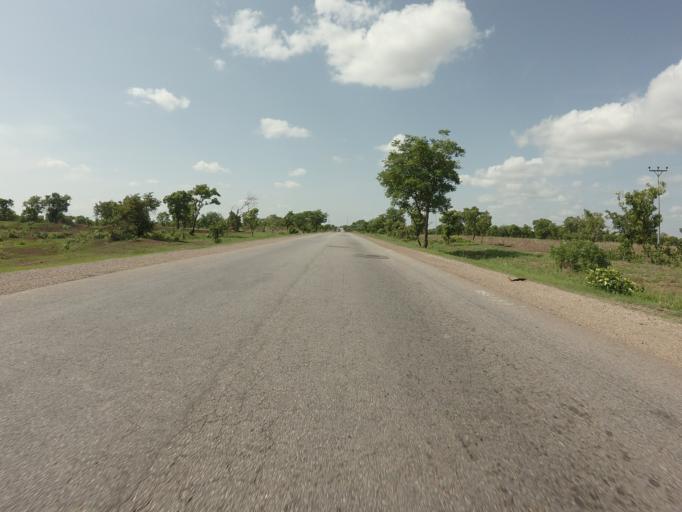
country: GH
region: Northern
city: Savelugu
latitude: 9.9679
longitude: -0.8298
